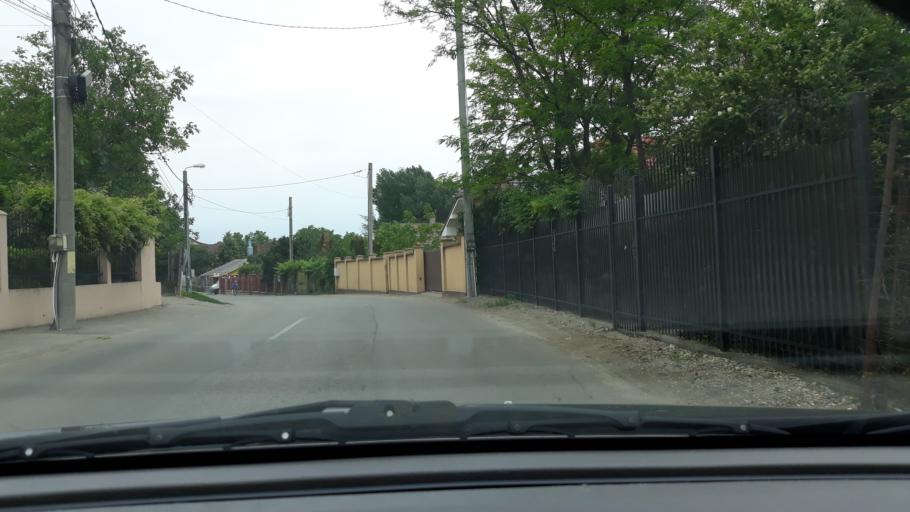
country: RO
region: Bihor
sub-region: Comuna Biharea
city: Oradea
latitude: 47.0519
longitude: 21.9712
